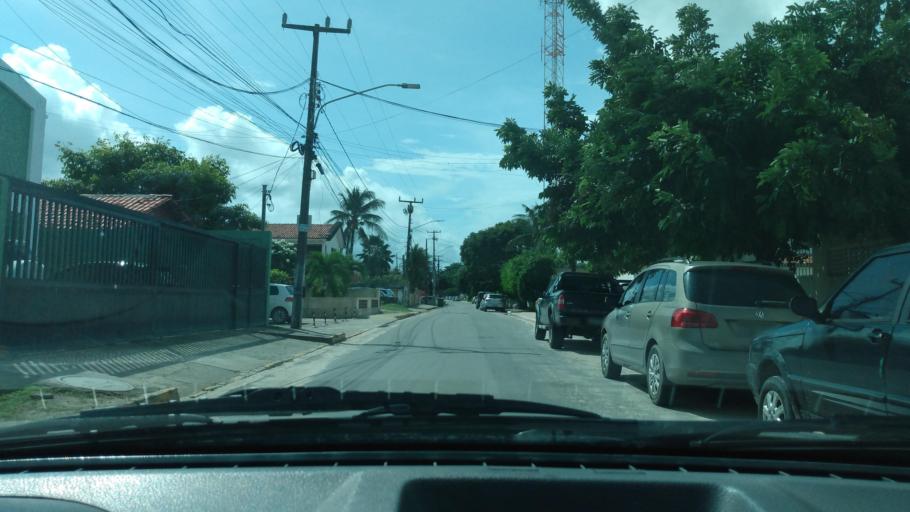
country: BR
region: Pernambuco
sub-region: Cabo De Santo Agostinho
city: Cabo
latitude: -8.3356
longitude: -34.9514
